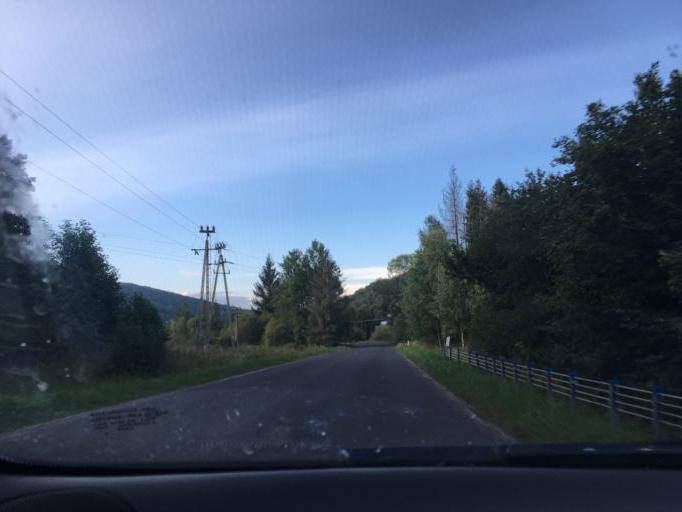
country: PL
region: Subcarpathian Voivodeship
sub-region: Powiat leski
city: Cisna
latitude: 49.1896
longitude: 22.4265
